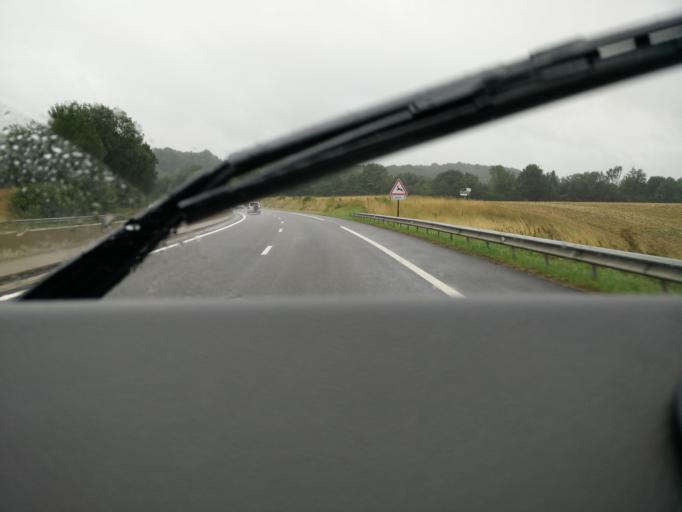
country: FR
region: Nord-Pas-de-Calais
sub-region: Departement du Pas-de-Calais
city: Saint-Pol-sur-Ternoise
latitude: 50.3682
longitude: 2.3030
